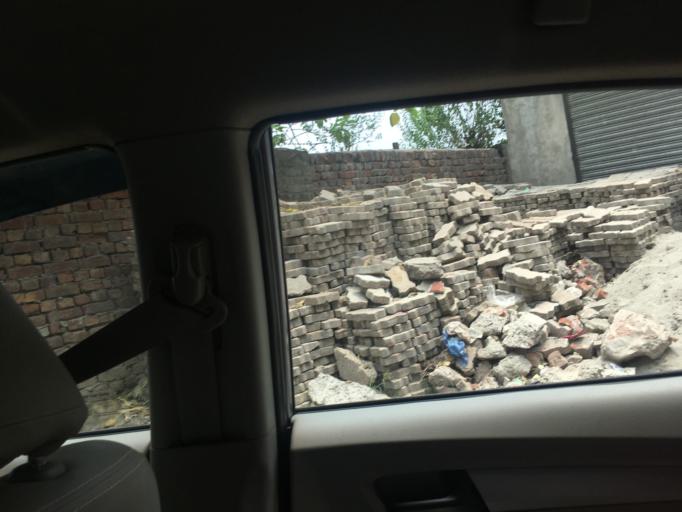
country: PK
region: Punjab
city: Lahore
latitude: 31.6126
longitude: 74.3524
